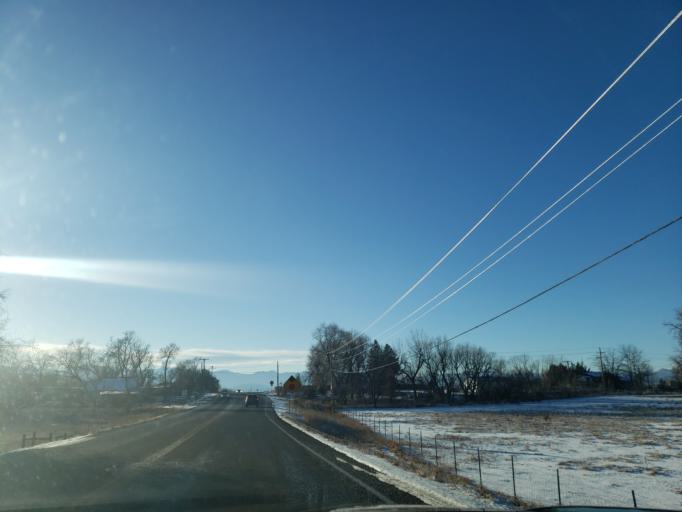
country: US
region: Colorado
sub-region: Larimer County
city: Fort Collins
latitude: 40.6395
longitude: -105.0702
